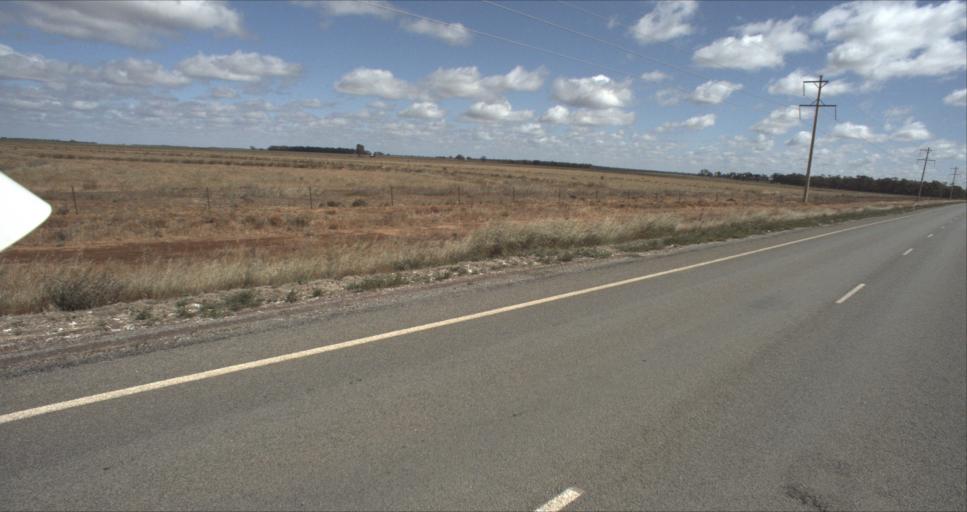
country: AU
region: New South Wales
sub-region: Murrumbidgee Shire
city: Darlington Point
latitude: -34.5827
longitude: 146.1648
